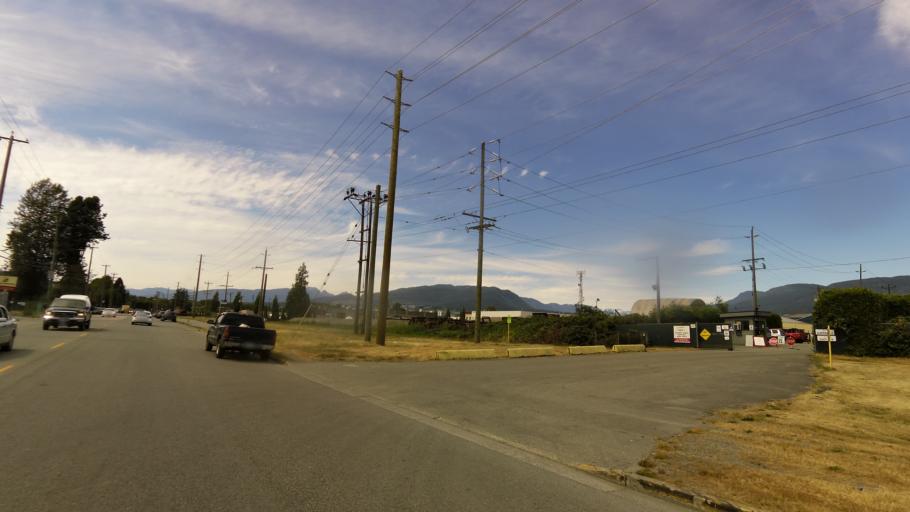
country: CA
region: British Columbia
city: Coquitlam
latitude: 49.2555
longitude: -122.7688
